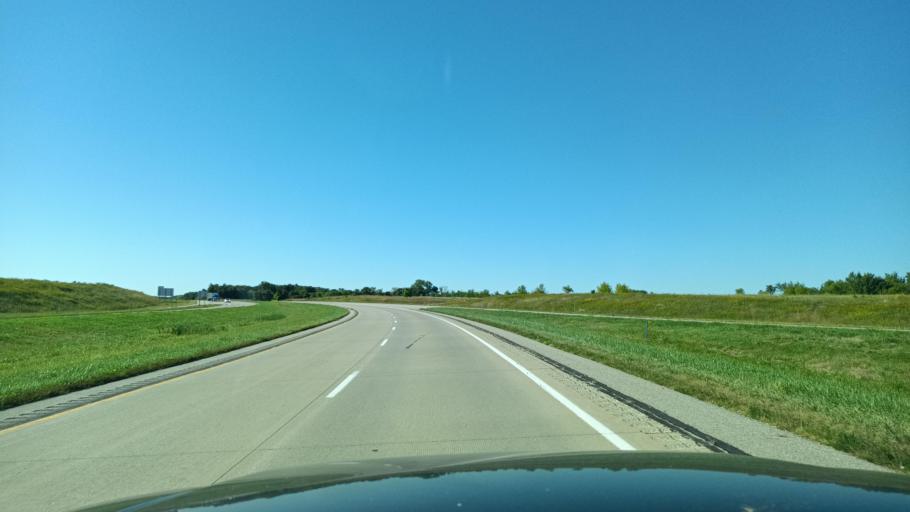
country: US
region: Iowa
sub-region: Lee County
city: Fort Madison
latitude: 40.6672
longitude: -91.3602
